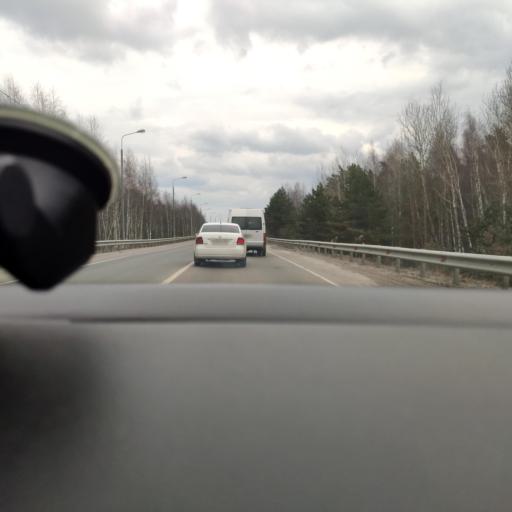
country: RU
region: Moskovskaya
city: Il'inskiy Pogost
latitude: 55.4878
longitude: 38.9032
